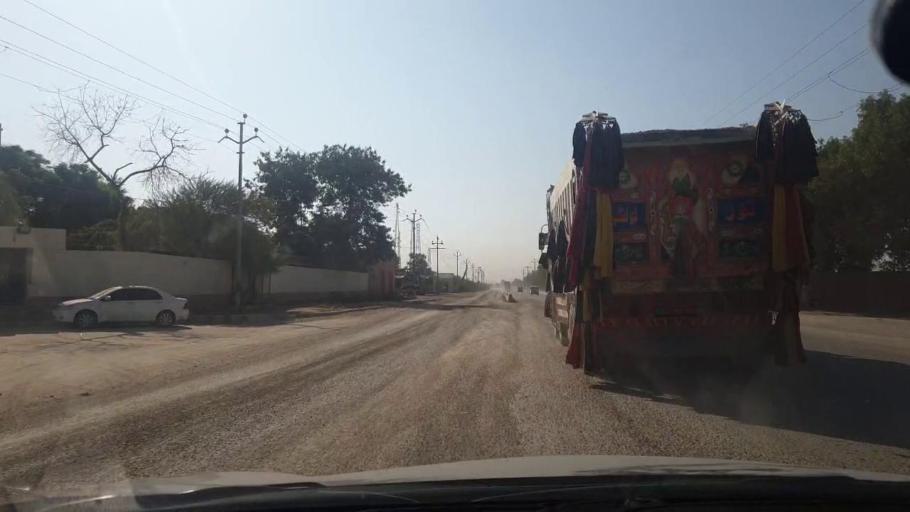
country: PK
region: Sindh
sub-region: Karachi District
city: Karachi
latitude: 25.0836
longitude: 67.0127
